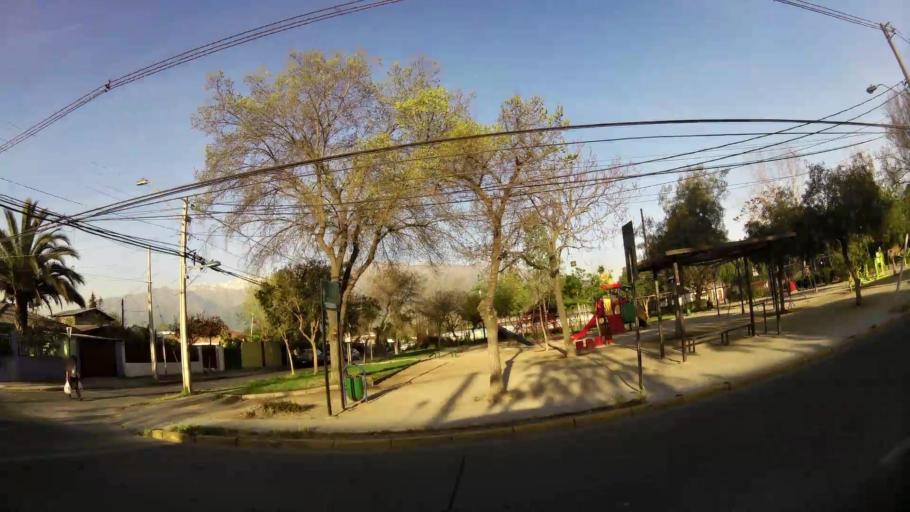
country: CL
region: Santiago Metropolitan
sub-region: Provincia de Santiago
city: La Pintana
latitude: -33.5484
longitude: -70.5829
